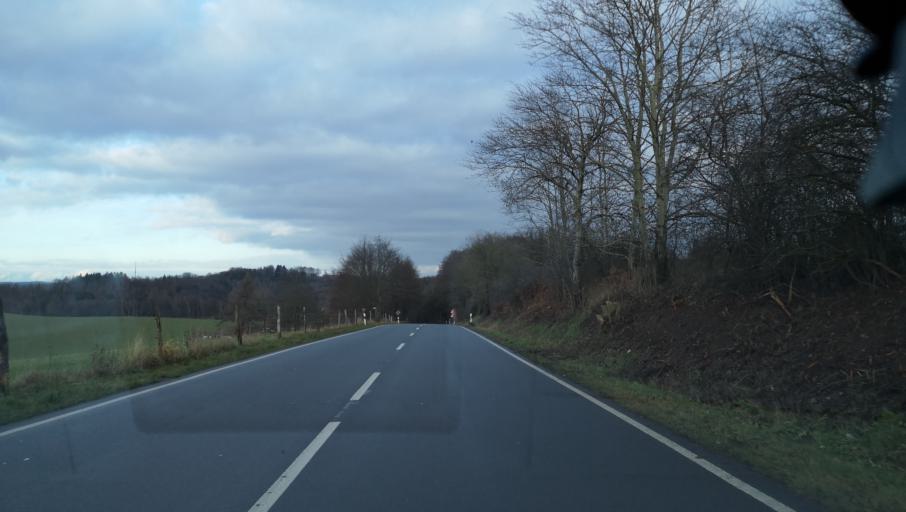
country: DE
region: North Rhine-Westphalia
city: Radevormwald
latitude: 51.2053
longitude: 7.3174
